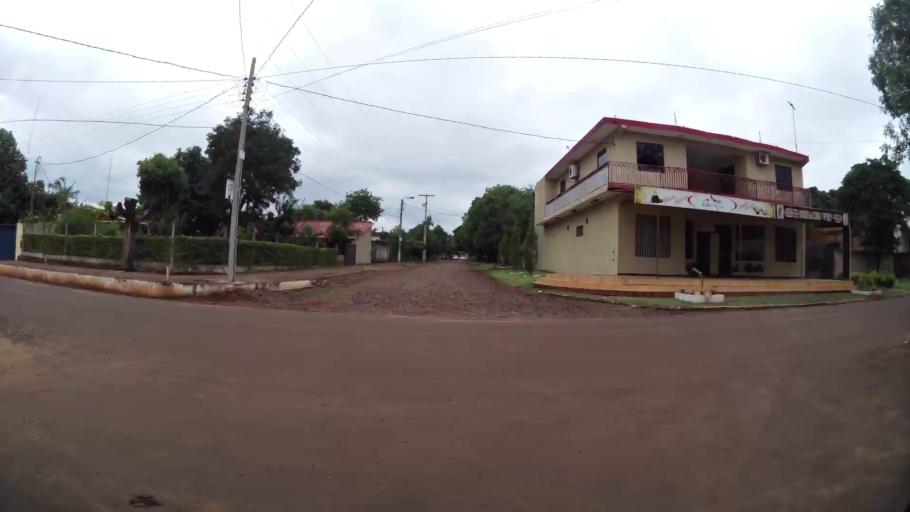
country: PY
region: Alto Parana
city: Presidente Franco
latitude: -25.4889
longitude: -54.7677
